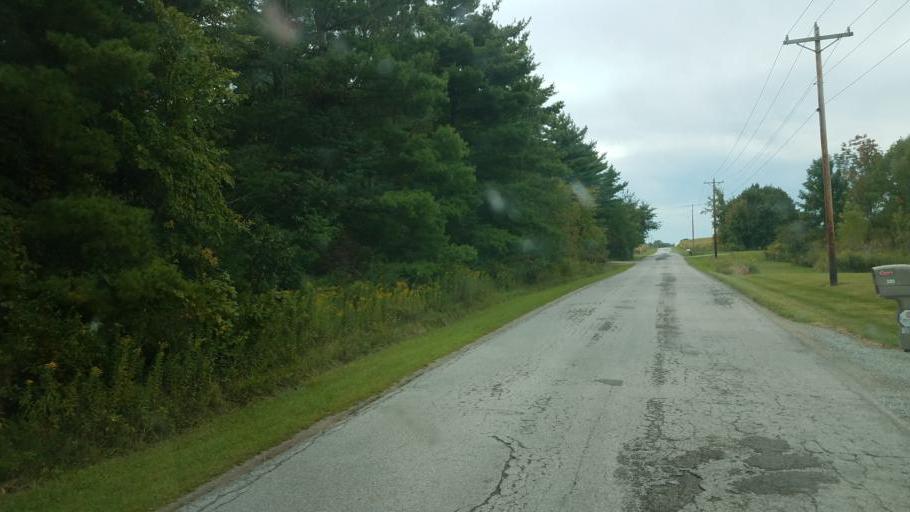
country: US
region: Ohio
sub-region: Knox County
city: Centerburg
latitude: 40.3560
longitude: -82.7253
